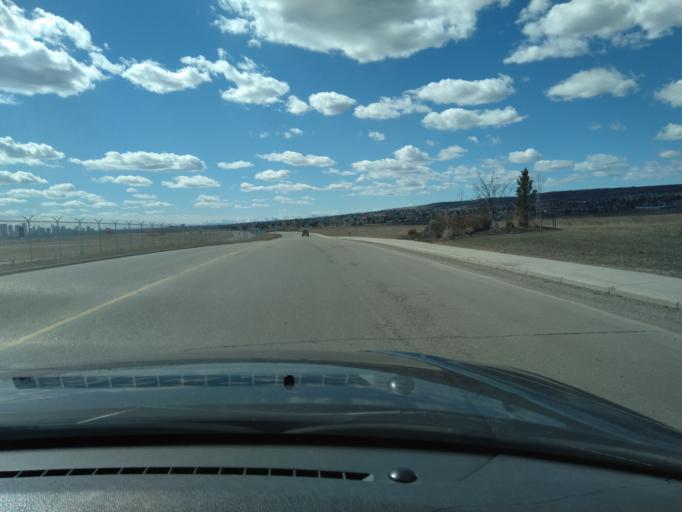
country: CA
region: Alberta
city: Calgary
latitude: 51.1304
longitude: -114.0391
